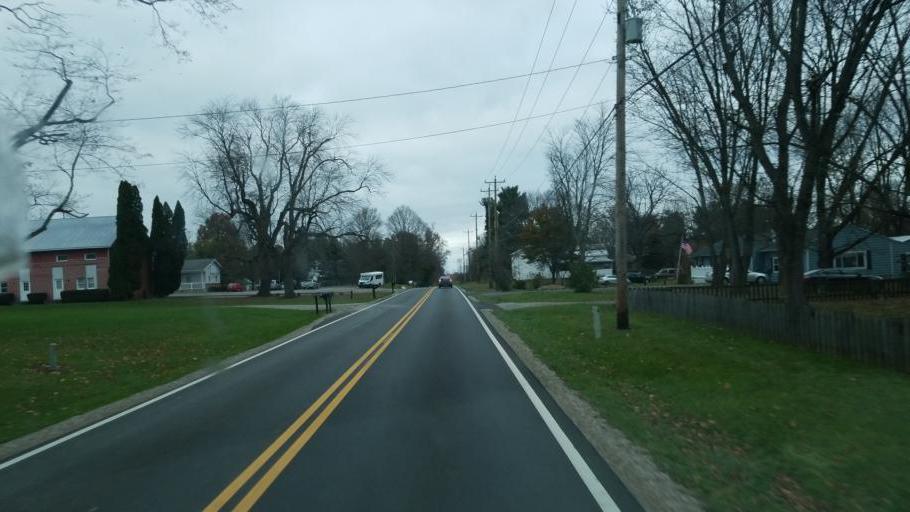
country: US
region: Ohio
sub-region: Delaware County
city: Sunbury
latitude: 40.2666
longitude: -82.9088
